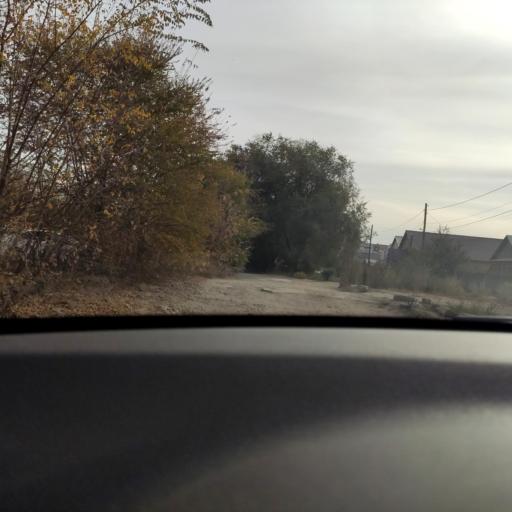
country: RU
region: Samara
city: Samara
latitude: 53.2197
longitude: 50.2183
